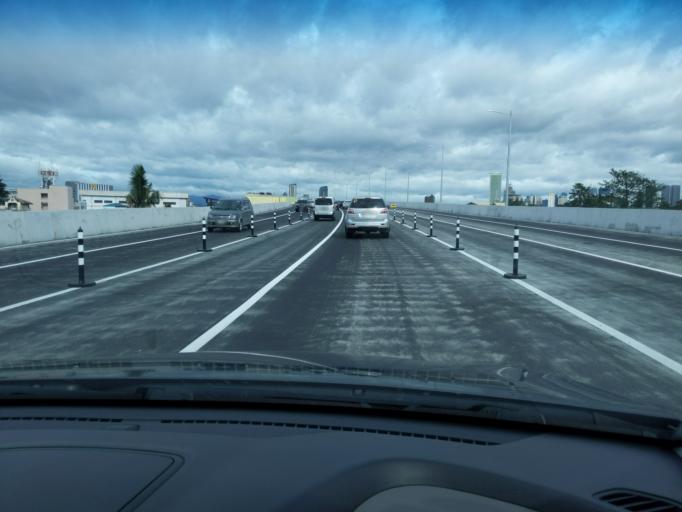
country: PH
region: Metro Manila
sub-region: San Juan
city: San Juan
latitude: 14.5889
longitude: 121.0194
